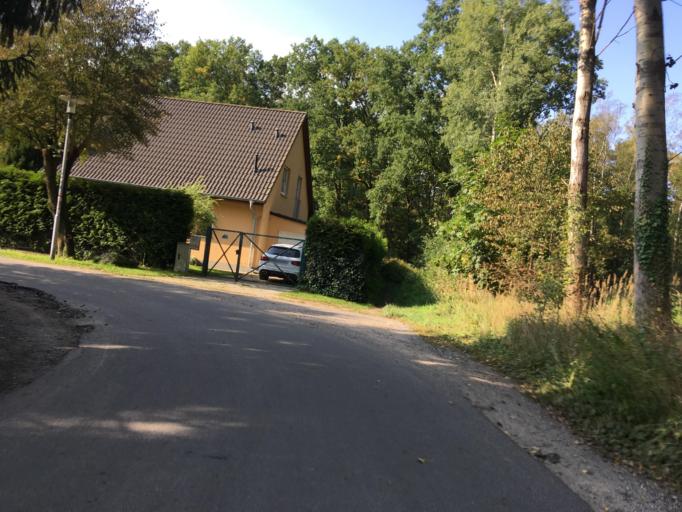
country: DE
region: Brandenburg
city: Wandlitz
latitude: 52.6846
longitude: 13.4352
